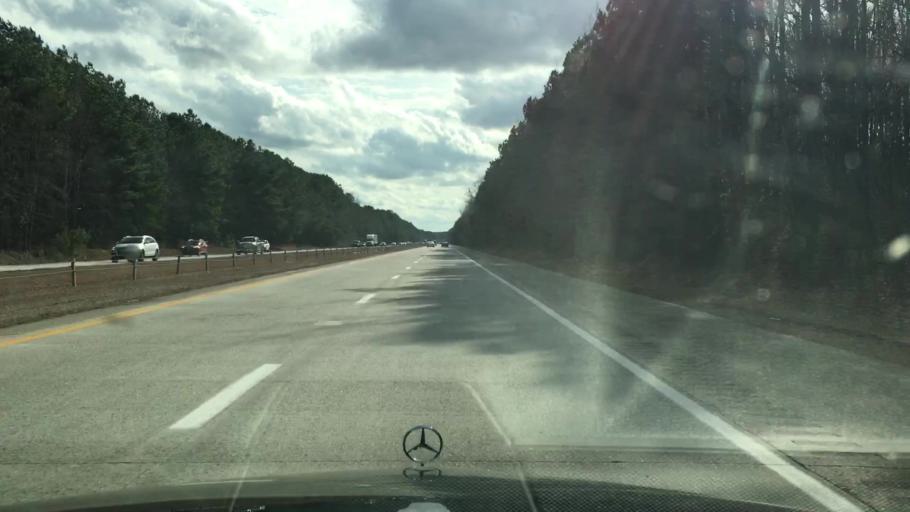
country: US
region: North Carolina
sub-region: Johnston County
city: Benson
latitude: 35.5030
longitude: -78.5547
